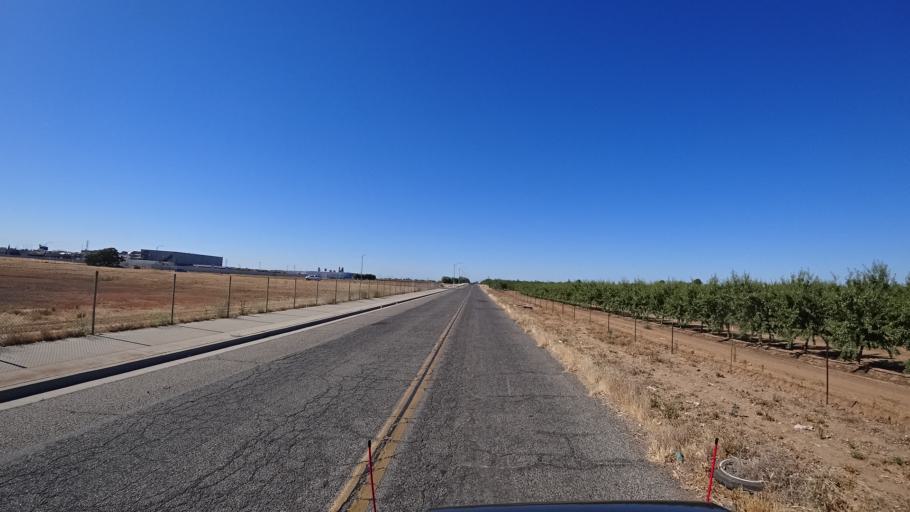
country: US
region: California
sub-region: Fresno County
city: West Park
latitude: 36.7186
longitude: -119.8267
